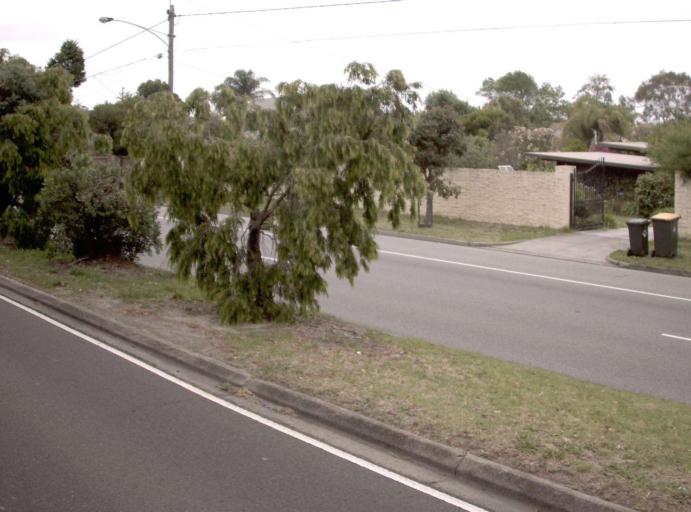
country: AU
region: Victoria
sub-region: Frankston
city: Frankston
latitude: -38.1627
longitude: 145.1027
